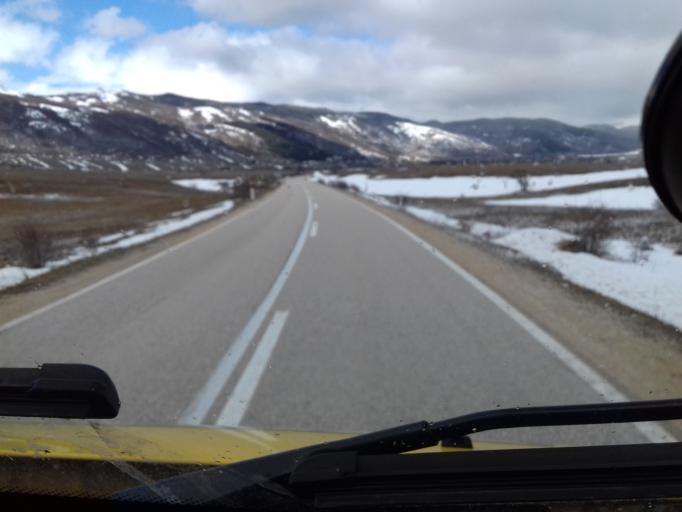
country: BA
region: Federation of Bosnia and Herzegovina
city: Tomislavgrad
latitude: 43.8126
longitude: 17.2031
